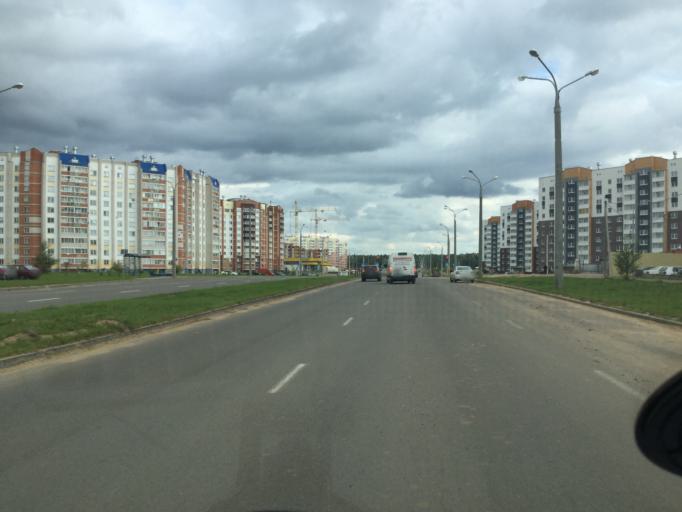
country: BY
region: Vitebsk
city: Vitebsk
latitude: 55.1646
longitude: 30.2690
